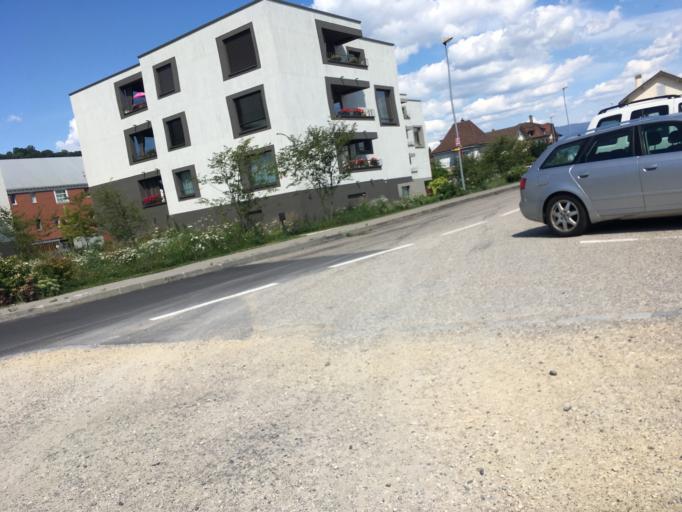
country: CH
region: Fribourg
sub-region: See District
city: Bas-Vully
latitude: 46.9634
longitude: 7.1200
